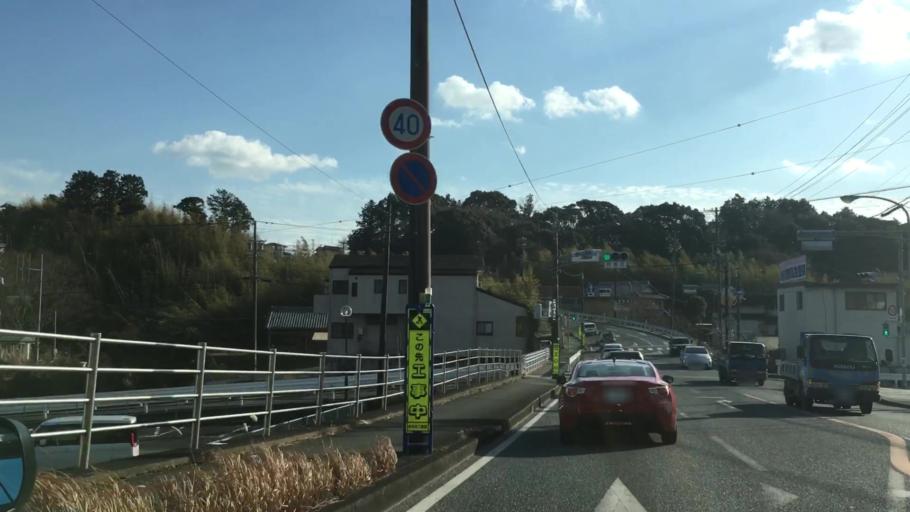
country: JP
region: Shizuoka
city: Hamamatsu
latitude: 34.7481
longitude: 137.6732
